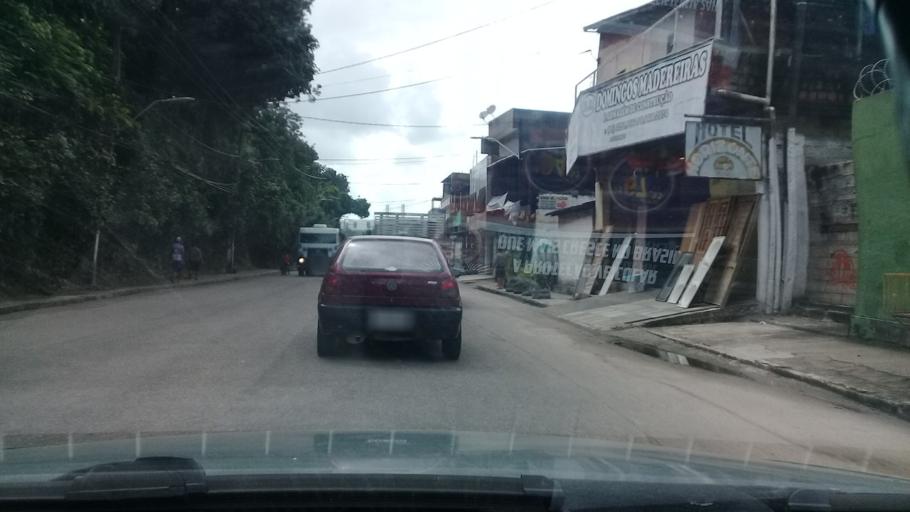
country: BR
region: Pernambuco
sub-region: Jaboatao Dos Guararapes
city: Jaboatao dos Guararapes
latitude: -8.1027
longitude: -34.9733
